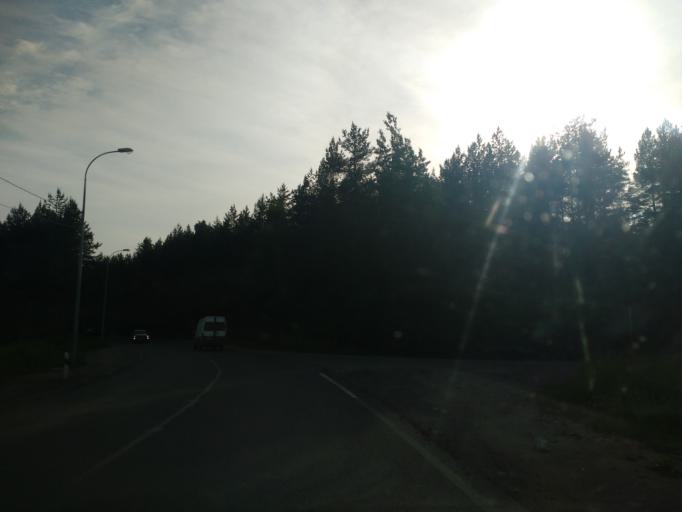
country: RU
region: Republic of Karelia
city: Petrozavodsk
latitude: 61.8391
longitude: 34.3132
